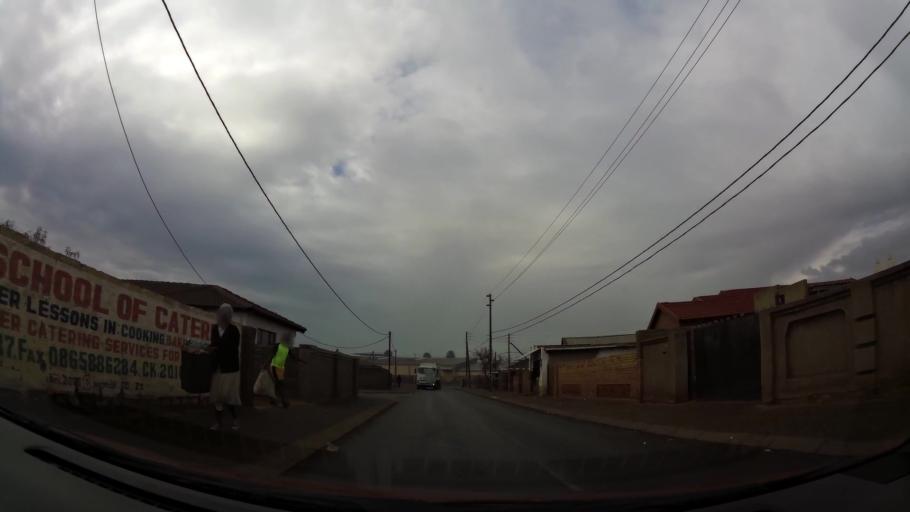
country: ZA
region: Gauteng
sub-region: City of Johannesburg Metropolitan Municipality
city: Soweto
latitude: -26.2853
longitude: 27.8469
